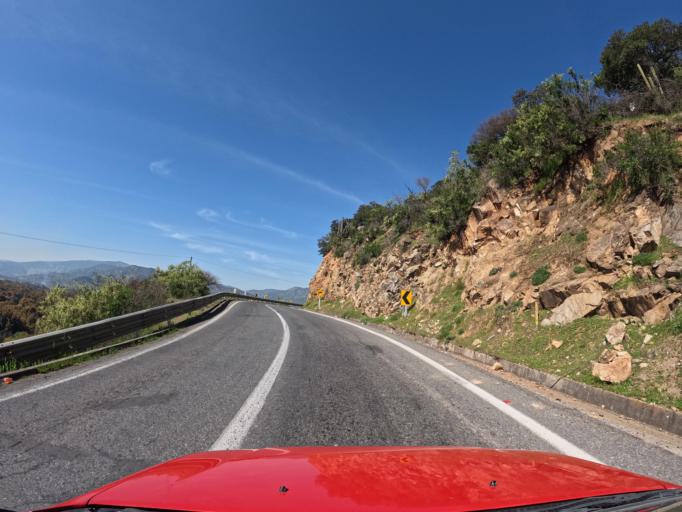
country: CL
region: Maule
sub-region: Provincia de Curico
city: Rauco
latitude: -35.0475
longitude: -71.5937
